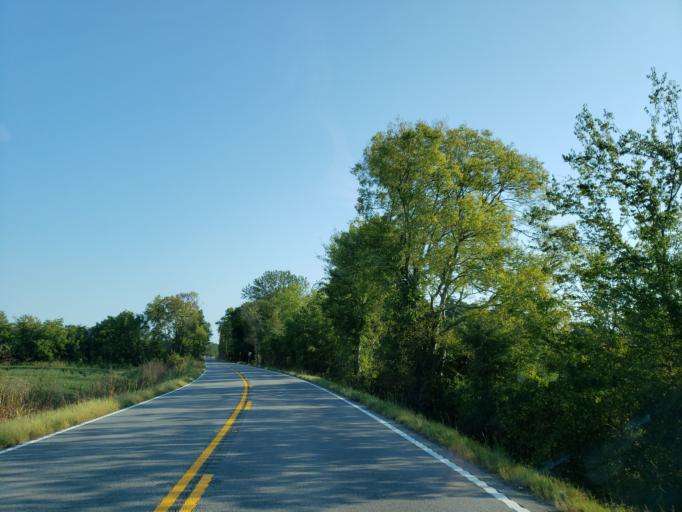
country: US
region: Tennessee
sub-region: Bradley County
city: Wildwood Lake
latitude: 34.9864
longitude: -84.7762
